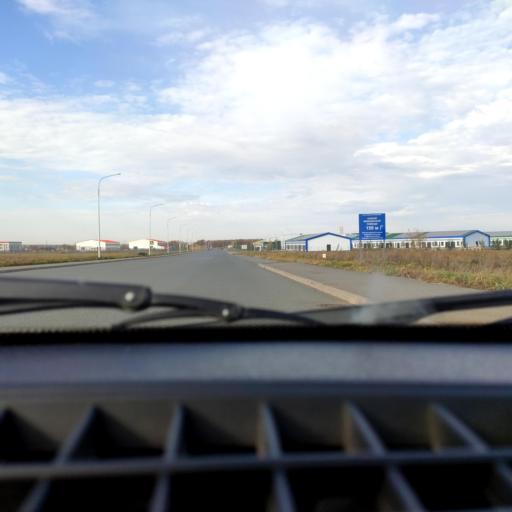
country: RU
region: Bashkortostan
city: Ufa
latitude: 54.6024
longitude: 55.9126
